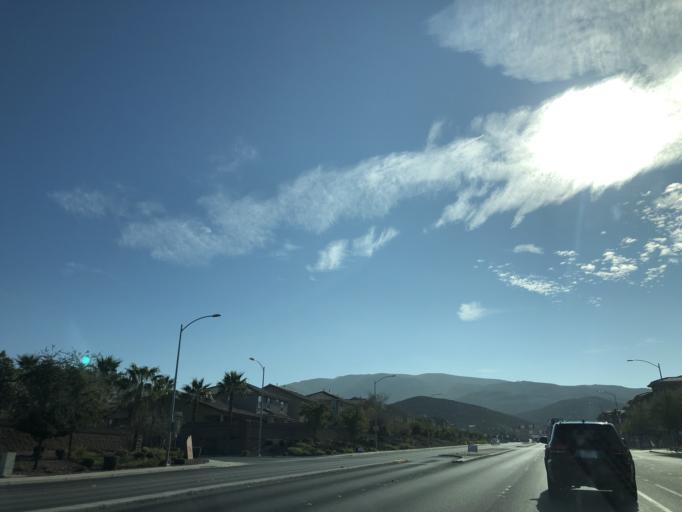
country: US
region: Nevada
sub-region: Clark County
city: Henderson
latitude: 36.0248
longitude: -115.0297
